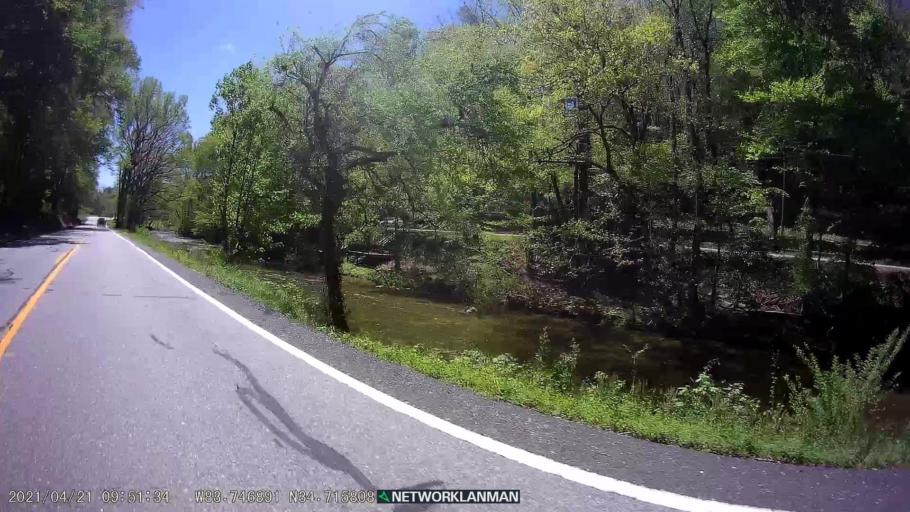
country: US
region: Georgia
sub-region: White County
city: Cleveland
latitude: 34.7157
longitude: -83.7468
